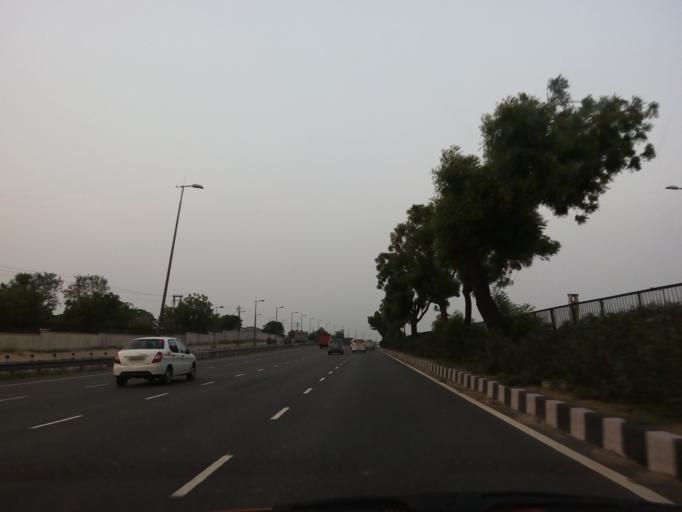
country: IN
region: NCT
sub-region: Central Delhi
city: Karol Bagh
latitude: 28.5615
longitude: 77.1338
